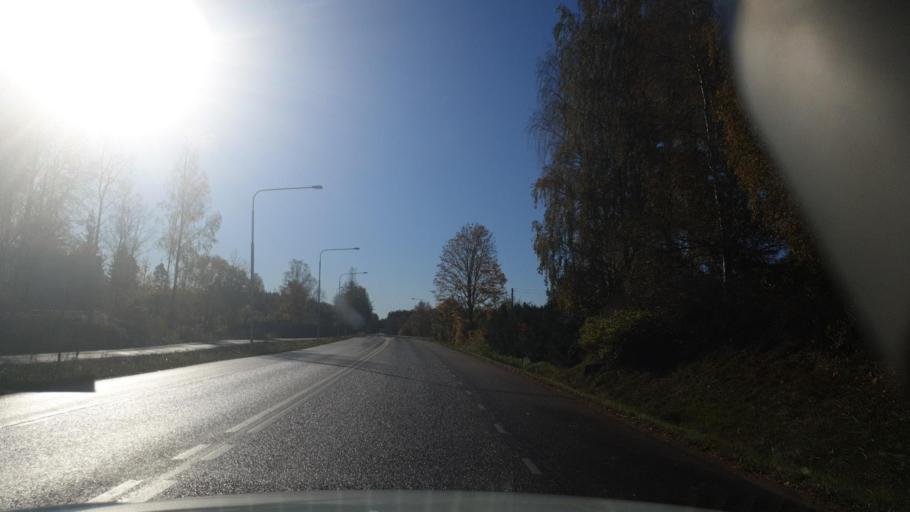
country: SE
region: Vaermland
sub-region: Arvika Kommun
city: Arvika
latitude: 59.6440
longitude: 12.6155
